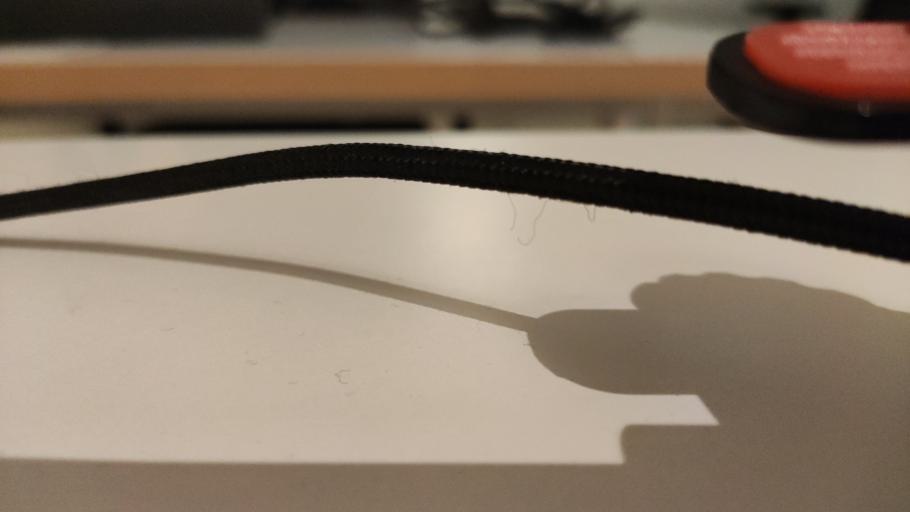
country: RU
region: Moskovskaya
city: Malino
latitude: 55.1118
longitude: 38.1642
